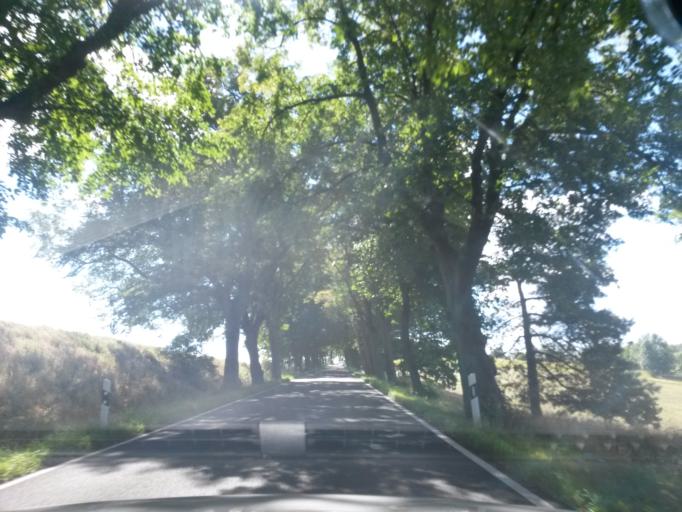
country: DE
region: Brandenburg
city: Schoneberg
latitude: 52.9912
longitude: 14.1013
